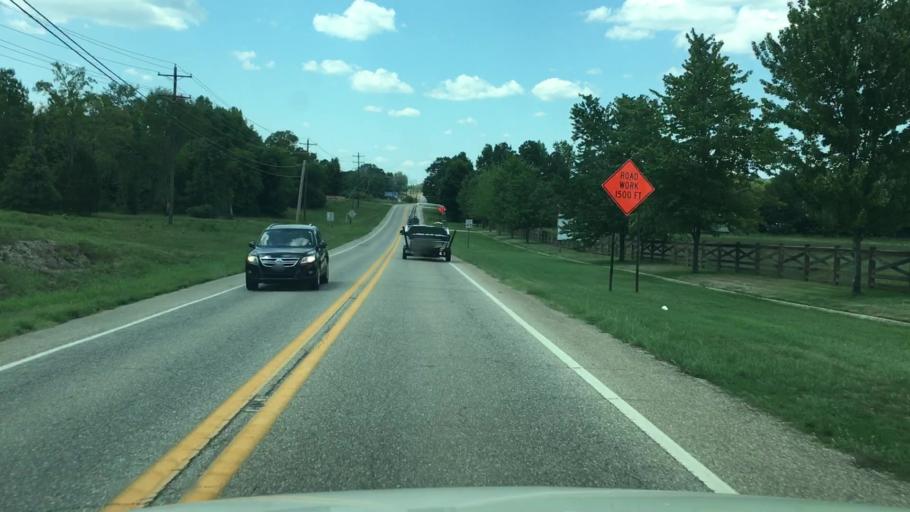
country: US
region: Arkansas
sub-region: Garland County
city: Lake Hamilton
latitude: 34.4081
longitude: -93.0918
